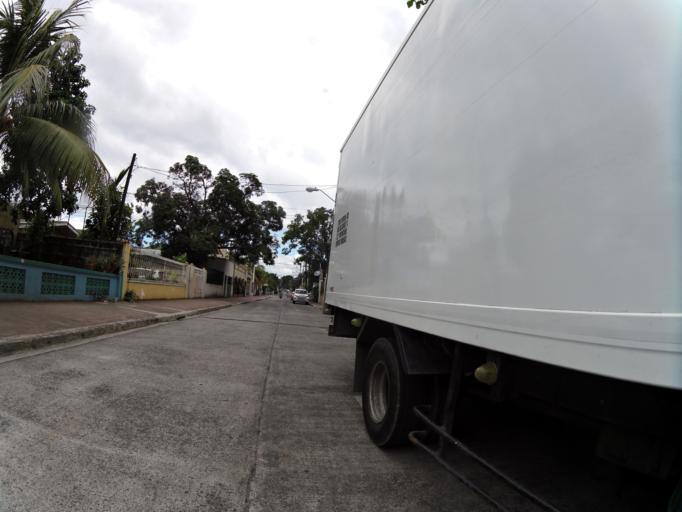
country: PH
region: Calabarzon
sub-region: Province of Rizal
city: Antipolo
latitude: 14.6396
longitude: 121.1154
